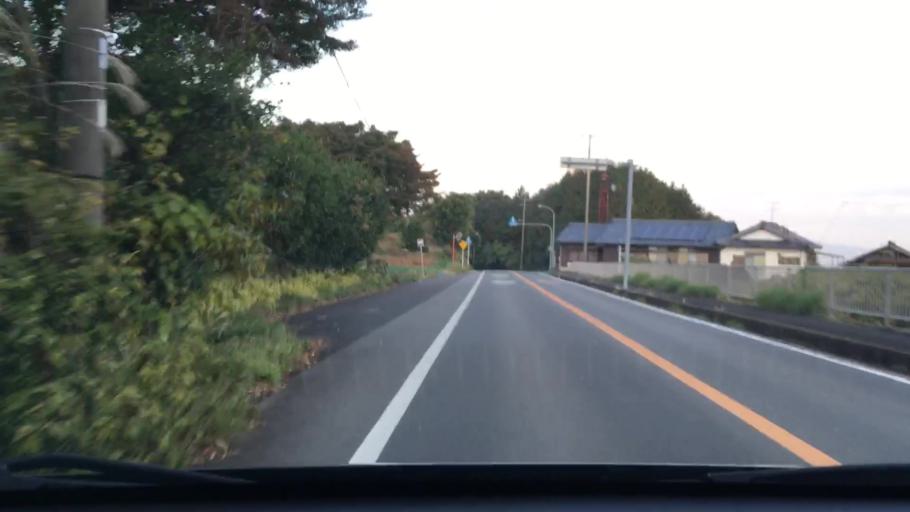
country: JP
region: Nagasaki
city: Sasebo
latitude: 33.0456
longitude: 129.7096
